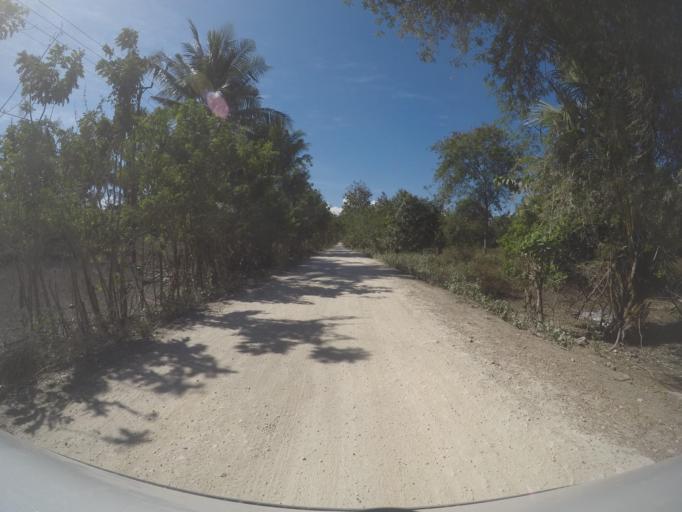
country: TL
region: Viqueque
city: Viqueque
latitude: -8.8825
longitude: 126.5073
